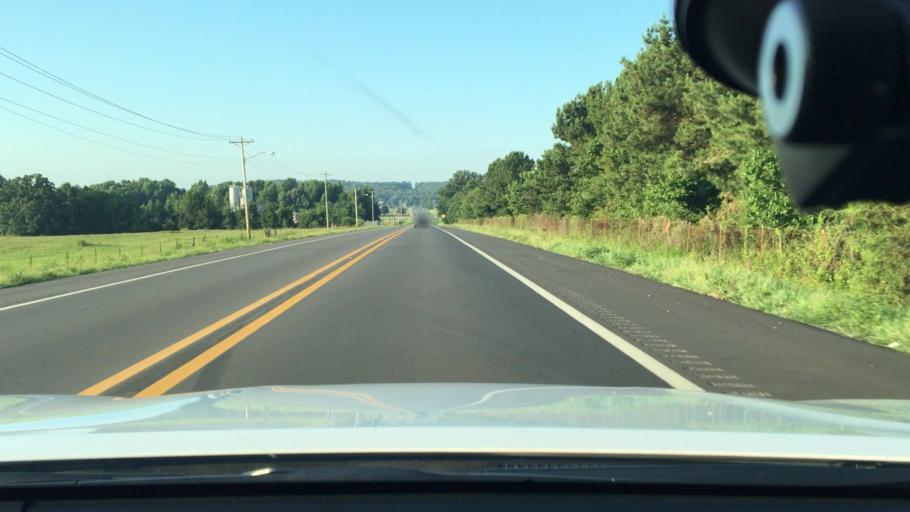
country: US
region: Arkansas
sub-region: Johnson County
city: Clarksville
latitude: 35.4393
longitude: -93.5292
